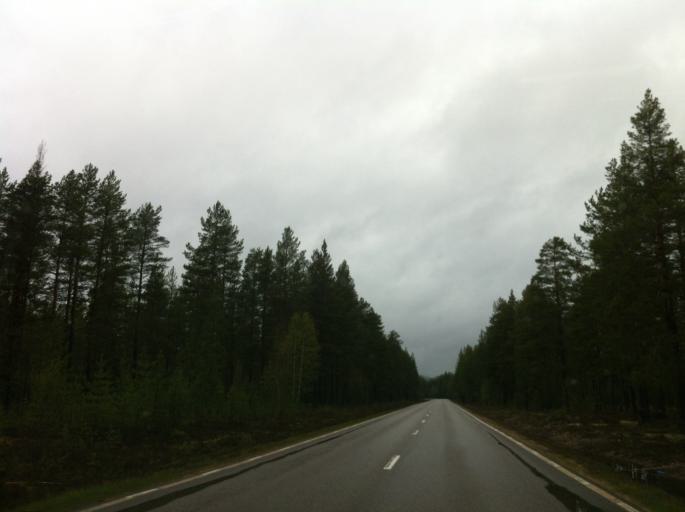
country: SE
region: Jaemtland
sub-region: Harjedalens Kommun
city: Sveg
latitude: 62.1422
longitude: 13.9788
